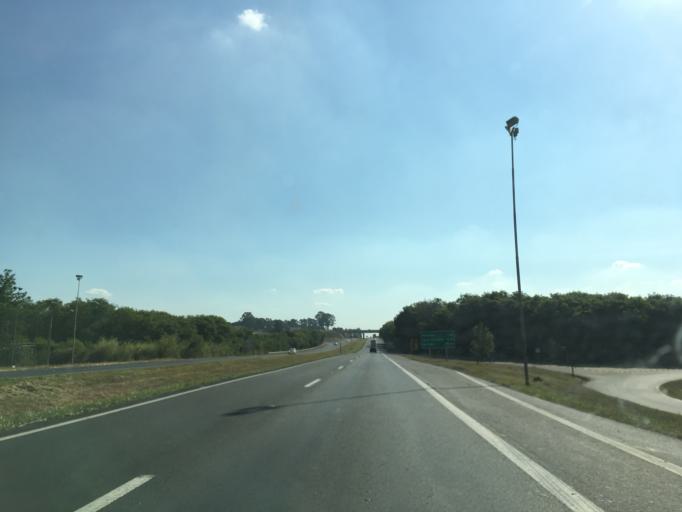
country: BR
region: Sao Paulo
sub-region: Piracicaba
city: Piracicaba
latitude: -22.7223
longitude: -47.5999
